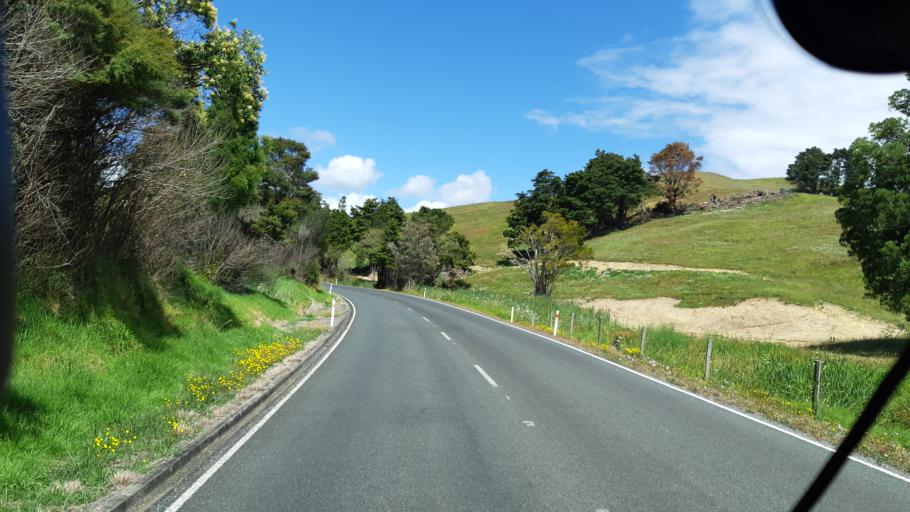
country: NZ
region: Northland
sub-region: Far North District
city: Kaitaia
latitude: -35.2701
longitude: 173.4873
